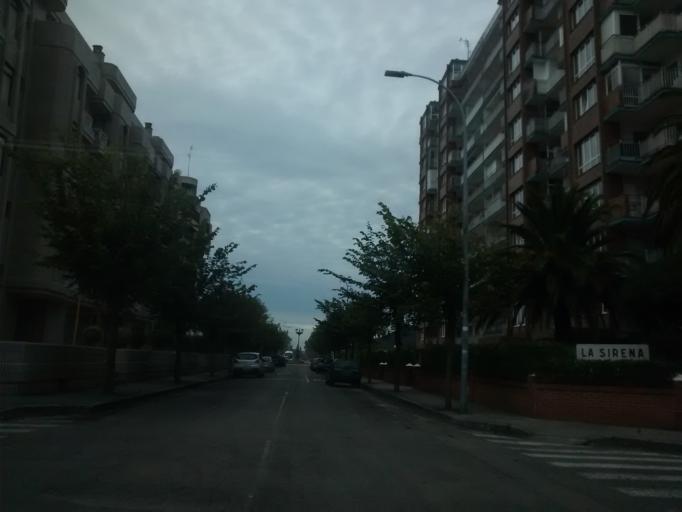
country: ES
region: Cantabria
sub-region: Provincia de Cantabria
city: Santona
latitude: 43.4275
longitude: -3.4480
